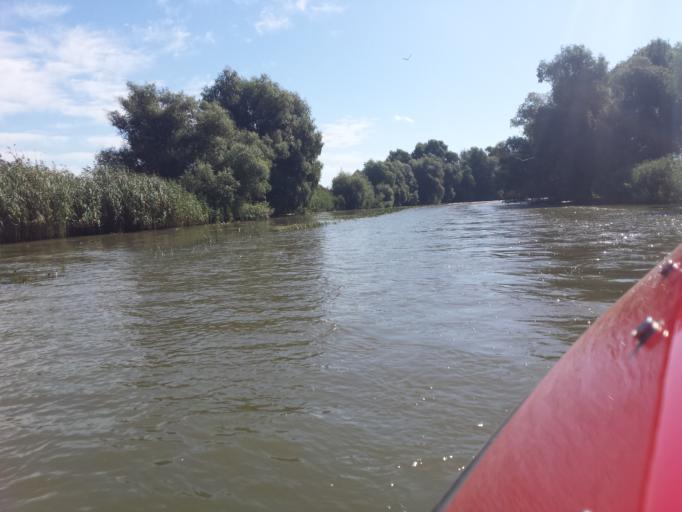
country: RO
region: Tulcea
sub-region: Comuna Pardina
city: Pardina
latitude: 45.2380
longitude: 29.0998
